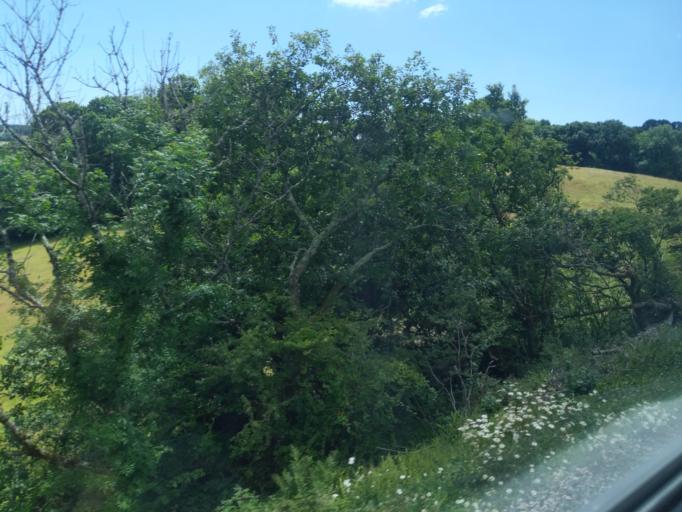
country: GB
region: England
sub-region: Cornwall
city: Pillaton
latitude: 50.3949
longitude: -4.2928
